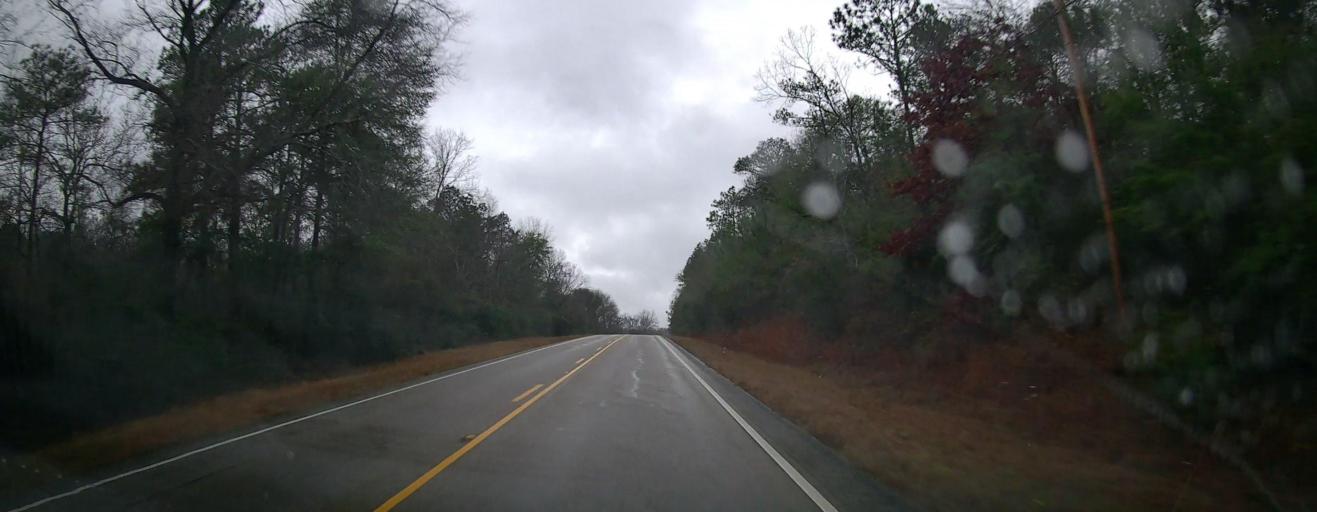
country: US
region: Alabama
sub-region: Autauga County
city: Pine Level
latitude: 32.5223
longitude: -86.6206
